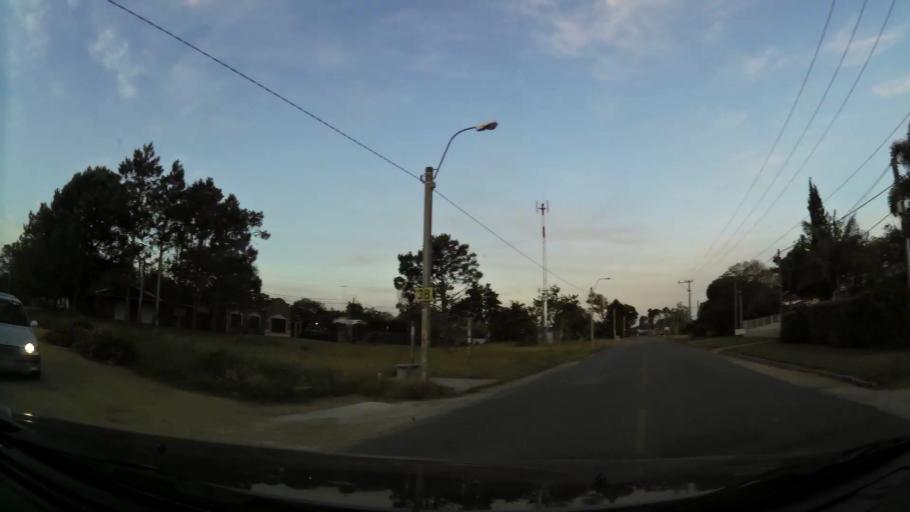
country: UY
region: Canelones
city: Atlantida
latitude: -34.7761
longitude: -55.7467
